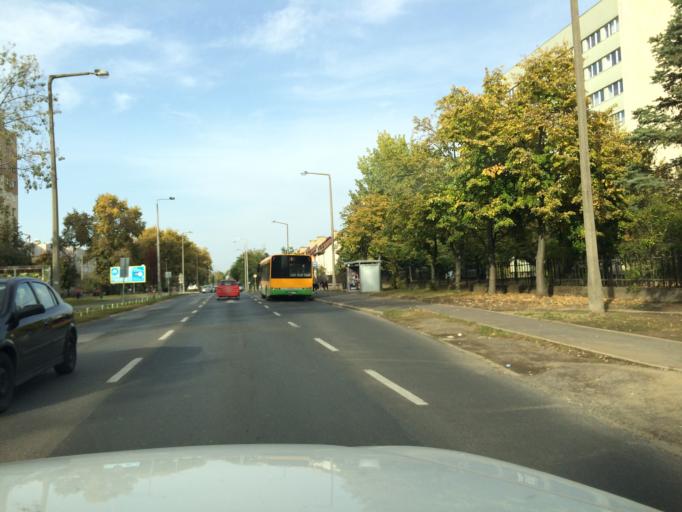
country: HU
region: Szabolcs-Szatmar-Bereg
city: Nyiregyhaza
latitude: 47.9736
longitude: 21.7262
